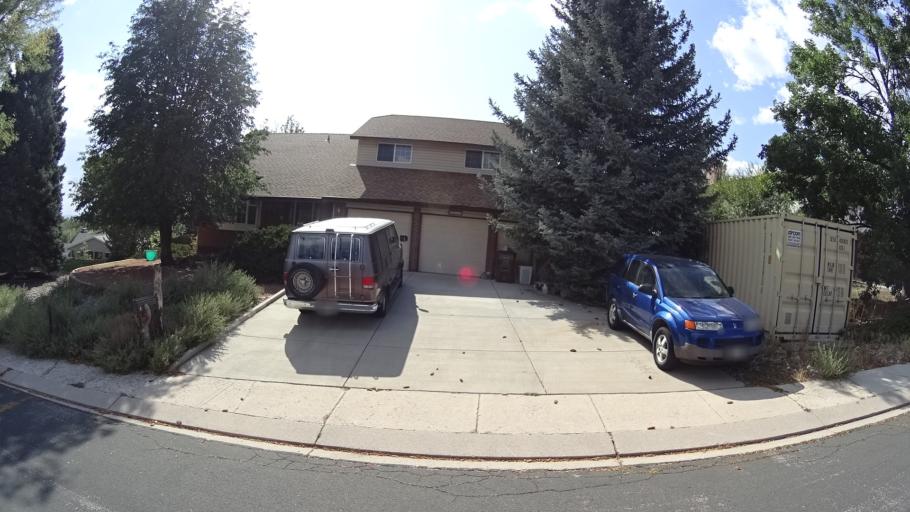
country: US
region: Colorado
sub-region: El Paso County
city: Cimarron Hills
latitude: 38.8711
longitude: -104.7292
